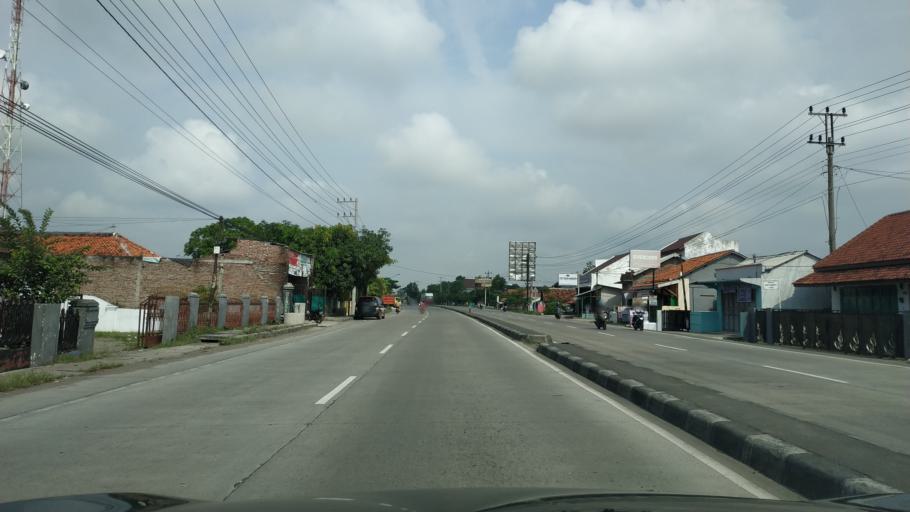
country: ID
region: Central Java
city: Bulakamba
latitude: -6.8734
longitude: 108.9434
